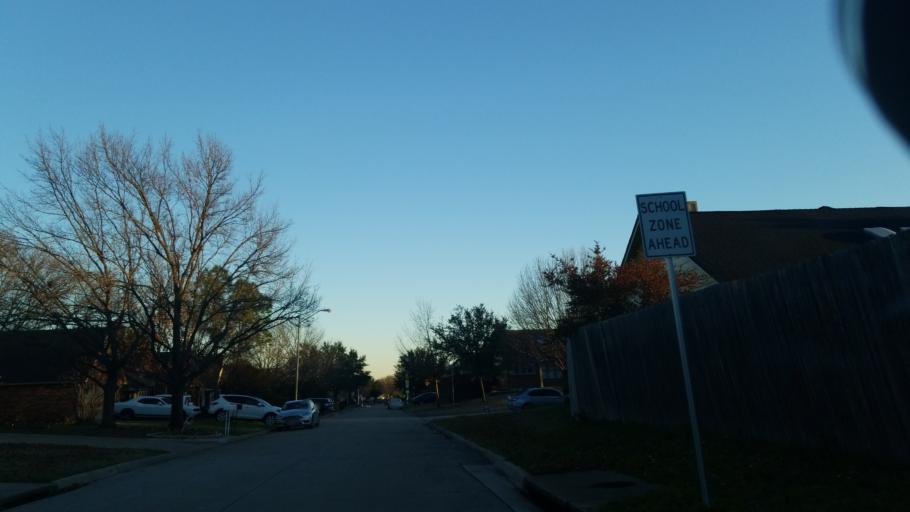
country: US
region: Texas
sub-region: Denton County
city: Hickory Creek
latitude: 33.1387
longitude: -97.0510
